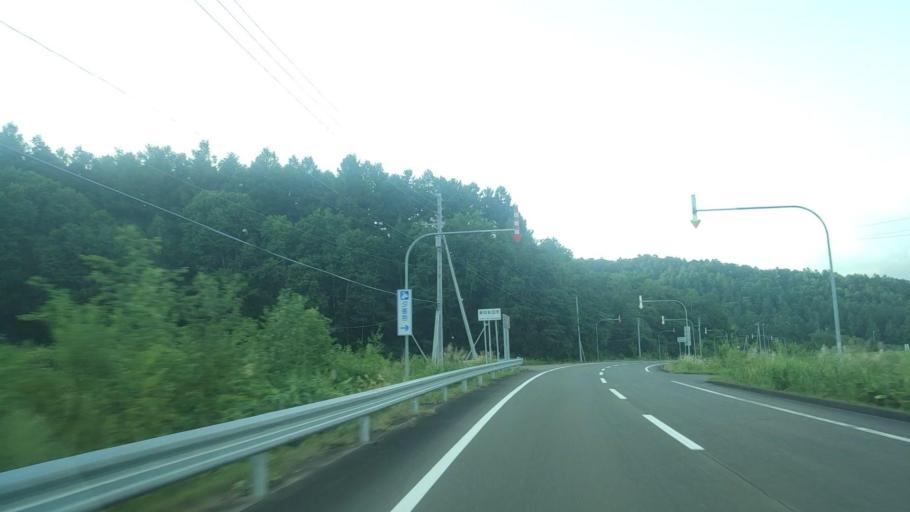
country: JP
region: Hokkaido
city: Bibai
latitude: 43.0622
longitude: 142.0994
